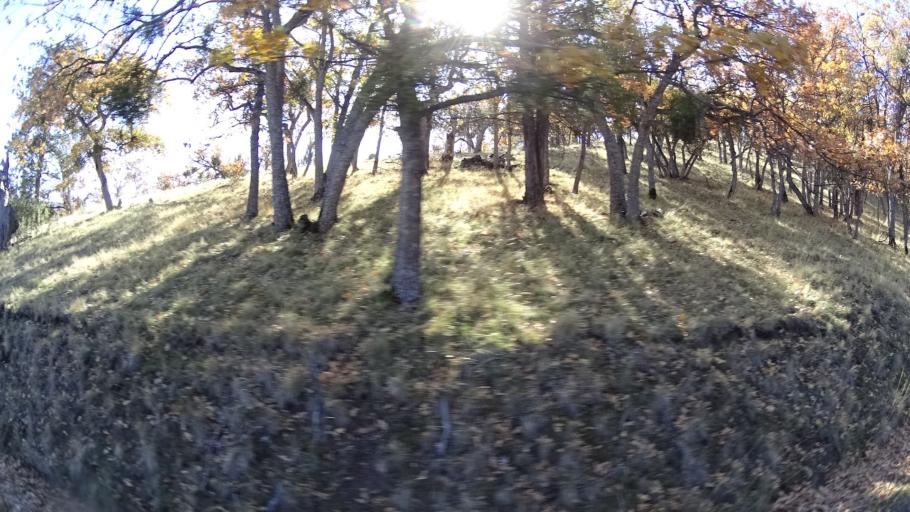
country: US
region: California
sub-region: Siskiyou County
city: Montague
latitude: 41.9810
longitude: -122.3098
